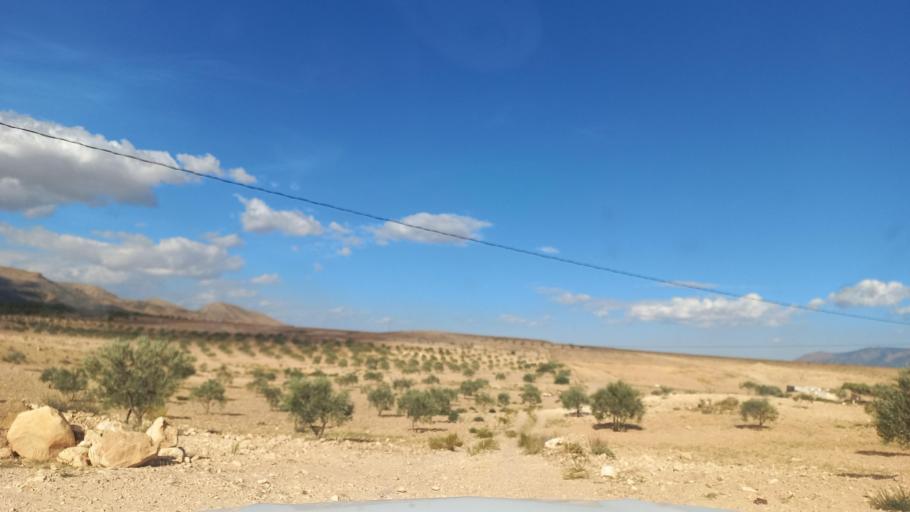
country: TN
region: Al Qasrayn
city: Sbiba
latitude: 35.4021
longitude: 9.0153
